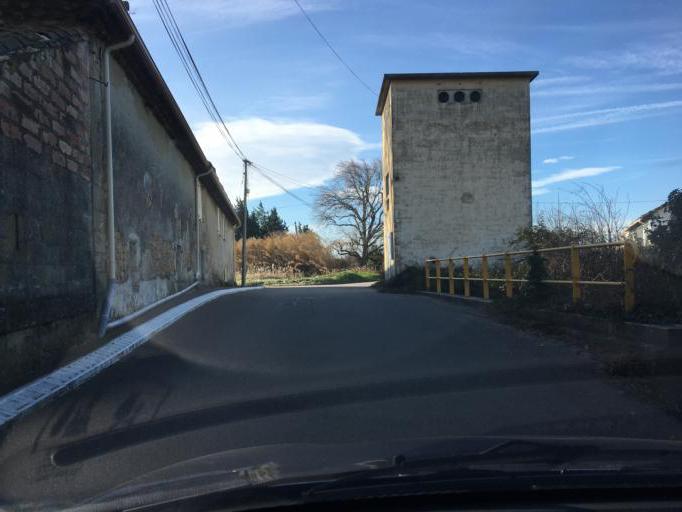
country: FR
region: Provence-Alpes-Cote d'Azur
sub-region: Departement du Vaucluse
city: Jonquieres
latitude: 44.1144
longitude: 4.8911
